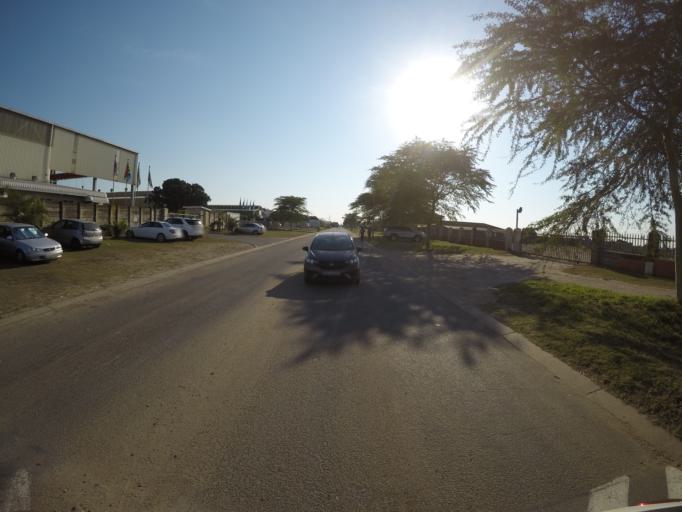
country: ZA
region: KwaZulu-Natal
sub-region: uThungulu District Municipality
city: Richards Bay
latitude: -28.7437
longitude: 32.0362
